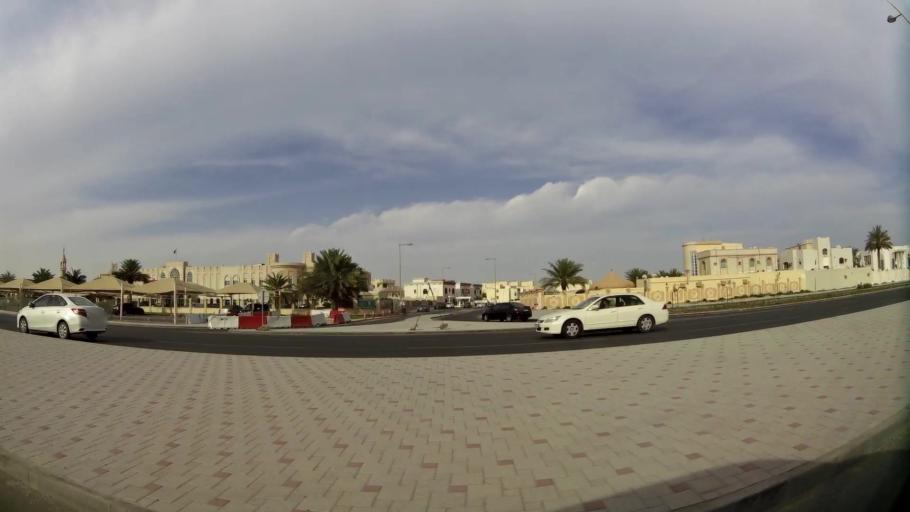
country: QA
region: Baladiyat ad Dawhah
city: Doha
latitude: 25.2502
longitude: 51.5384
